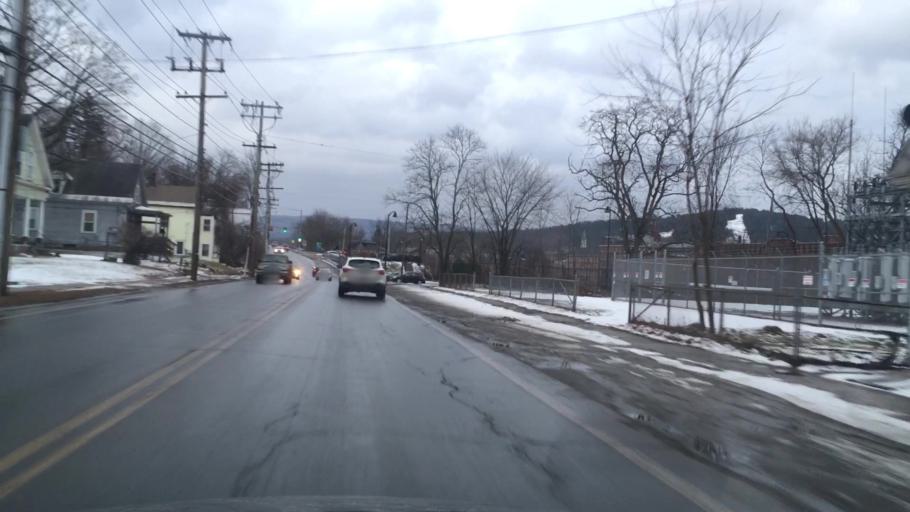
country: US
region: New Hampshire
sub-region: Sullivan County
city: Claremont
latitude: 43.3772
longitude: -72.3409
